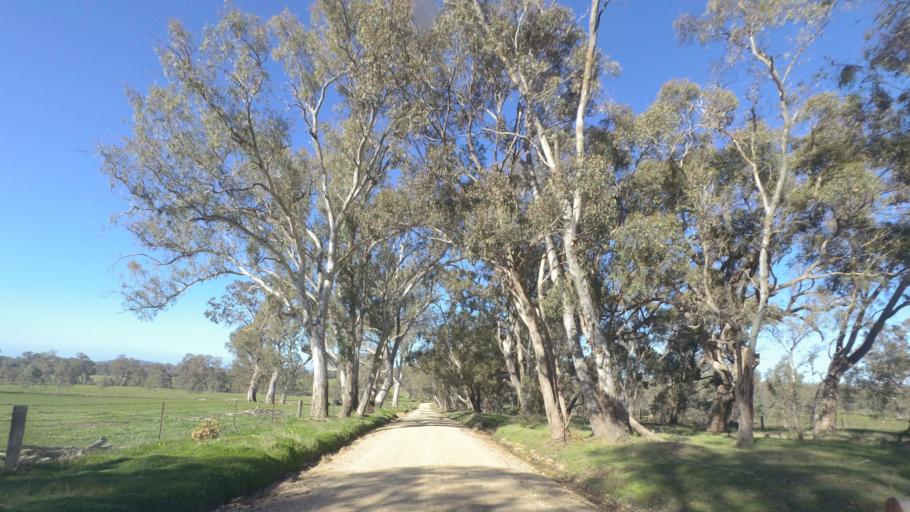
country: AU
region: Victoria
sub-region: Mount Alexander
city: Castlemaine
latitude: -36.9654
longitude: 144.3437
